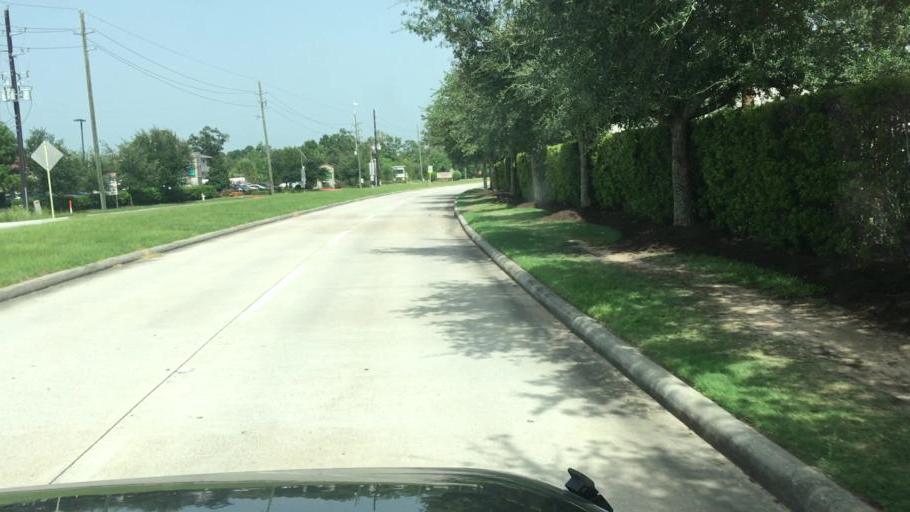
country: US
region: Texas
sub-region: Harris County
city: Atascocita
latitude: 29.9817
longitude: -95.1685
